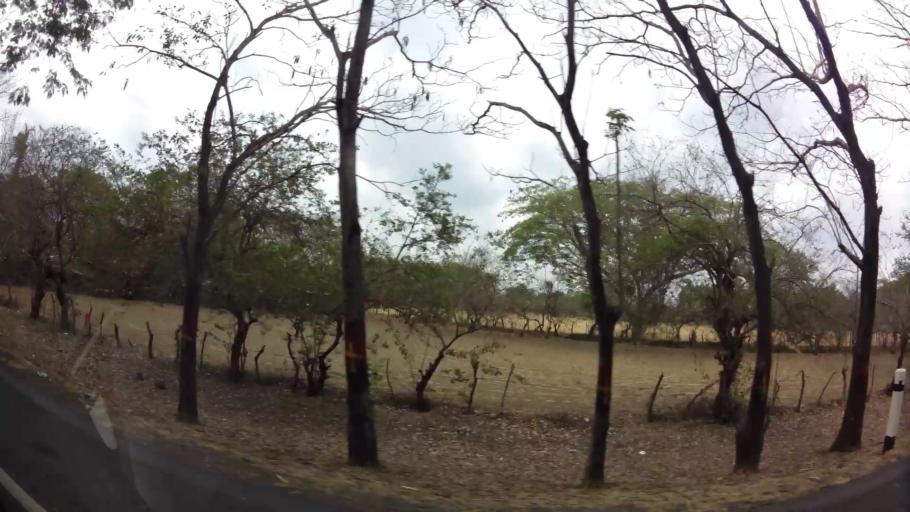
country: NI
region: Leon
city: Telica
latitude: 12.5128
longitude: -86.8614
